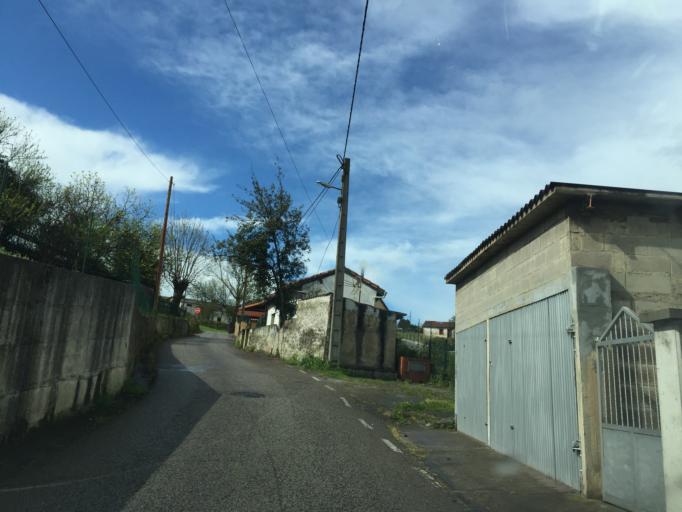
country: ES
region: Asturias
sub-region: Province of Asturias
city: Natahoyo
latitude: 43.5532
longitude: -5.7070
